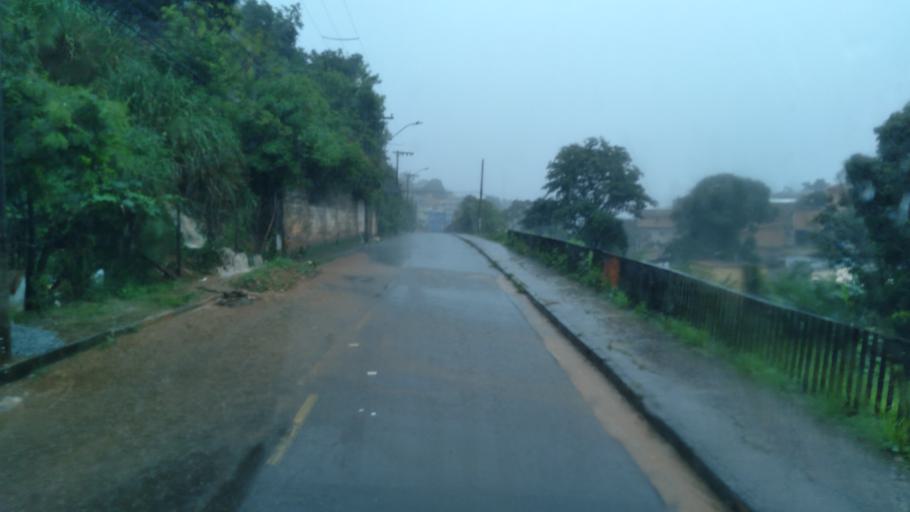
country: BR
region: Minas Gerais
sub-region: Belo Horizonte
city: Belo Horizonte
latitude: -19.9180
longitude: -43.8861
